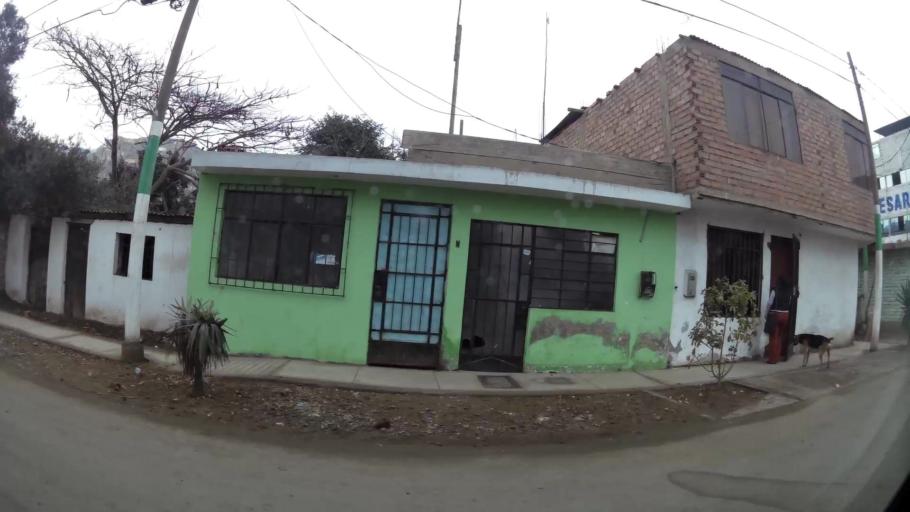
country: PE
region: Lima
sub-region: Lima
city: Urb. Santo Domingo
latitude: -11.8729
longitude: -77.0718
